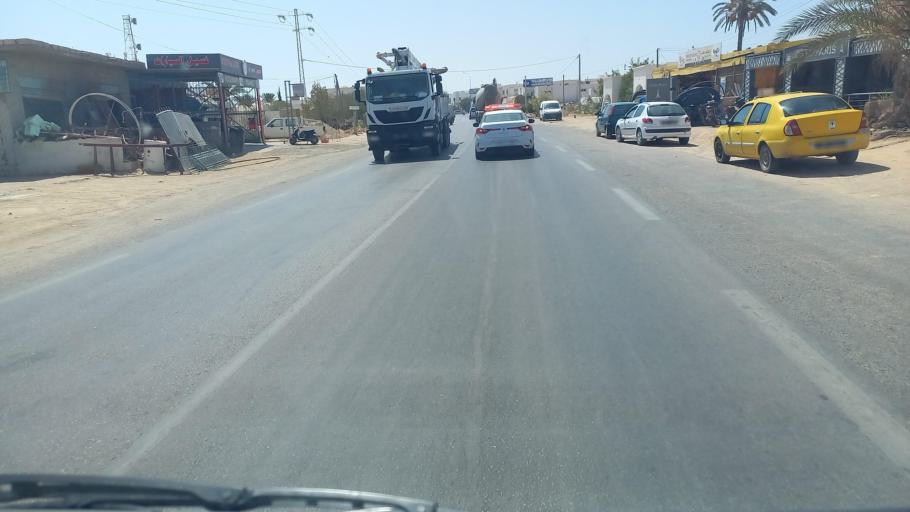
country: TN
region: Madanin
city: Houmt Souk
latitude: 33.8066
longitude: 10.8812
